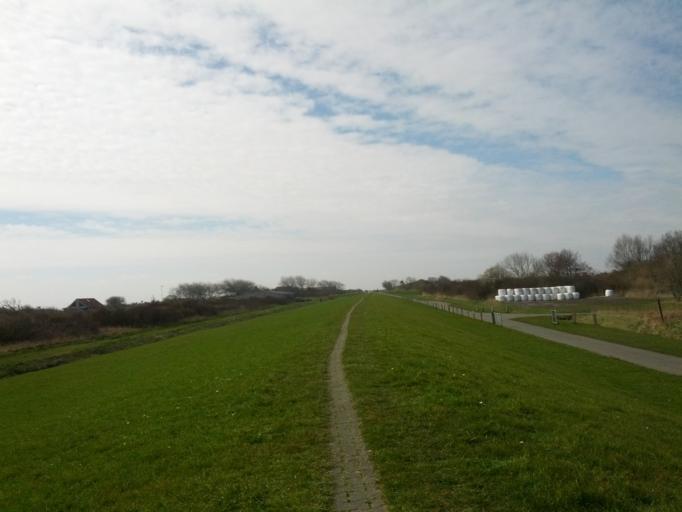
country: DE
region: Lower Saxony
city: Langeoog
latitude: 53.7321
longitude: 7.5014
